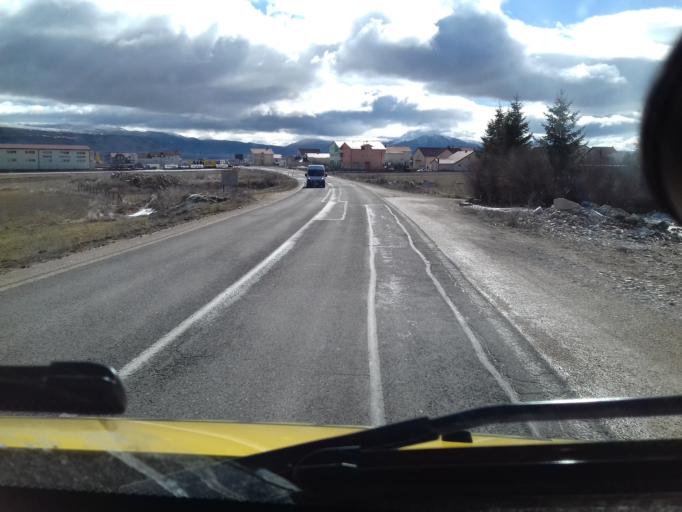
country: BA
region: Federation of Bosnia and Herzegovina
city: Tomislavgrad
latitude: 43.7203
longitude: 17.2315
